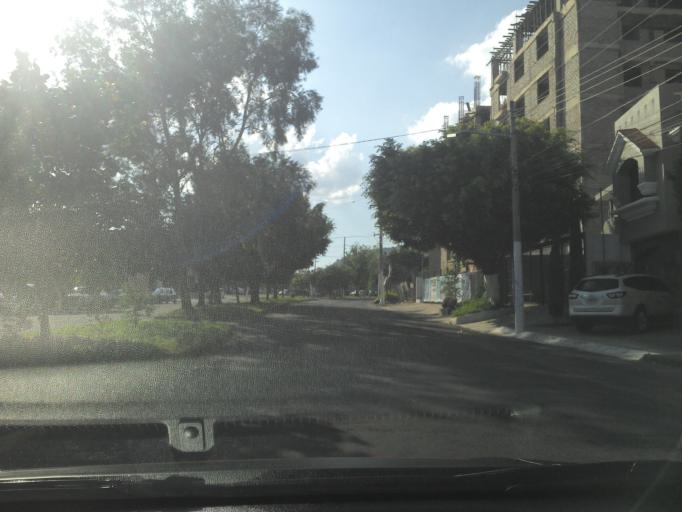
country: MX
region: Jalisco
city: Guadalajara
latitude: 20.6524
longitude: -103.4399
